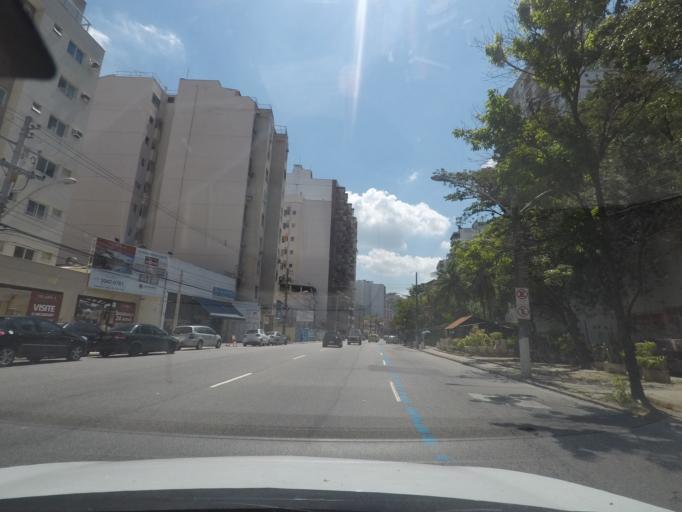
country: BR
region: Rio de Janeiro
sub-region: Rio De Janeiro
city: Rio de Janeiro
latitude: -22.9168
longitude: -43.2547
